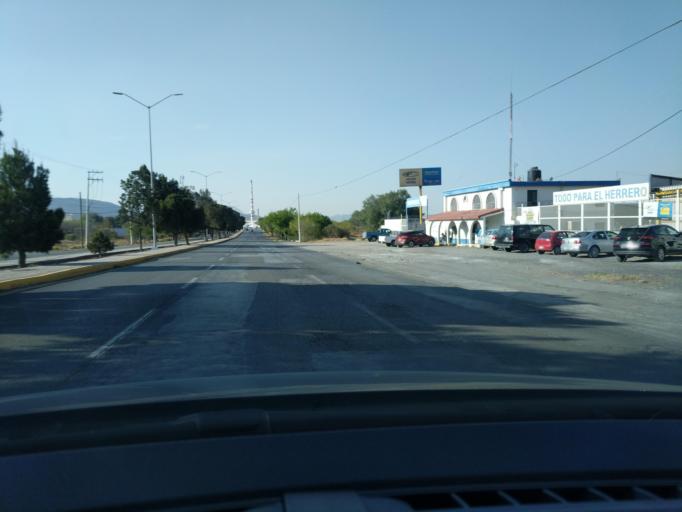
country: MX
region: Coahuila
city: Saltillo
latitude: 25.4739
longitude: -100.9826
